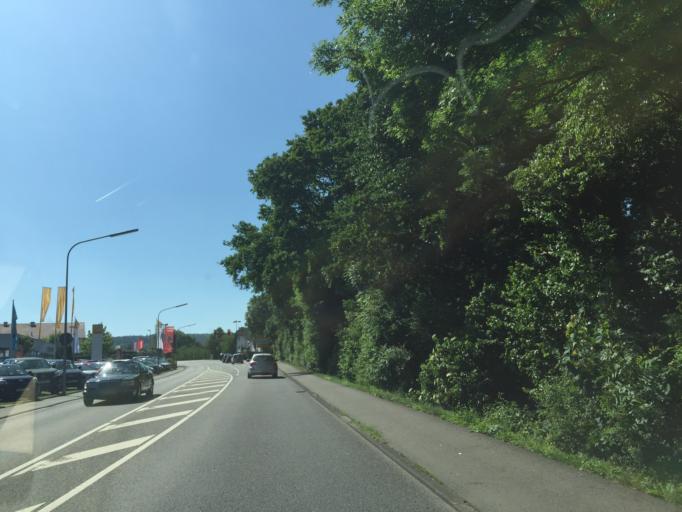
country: DE
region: Hesse
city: Michelstadt
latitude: 49.6663
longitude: 9.0056
